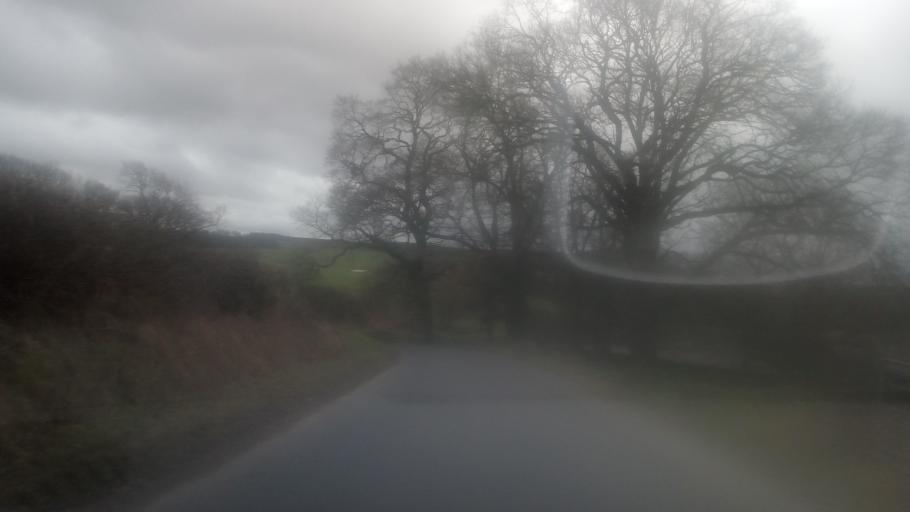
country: GB
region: Scotland
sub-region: The Scottish Borders
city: Jedburgh
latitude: 55.4933
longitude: -2.4793
